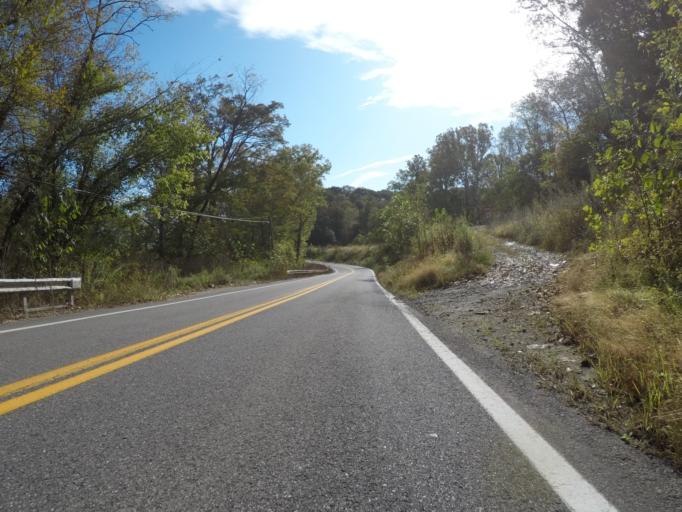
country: US
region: West Virginia
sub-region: Wayne County
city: Ceredo
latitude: 38.3676
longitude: -82.5406
